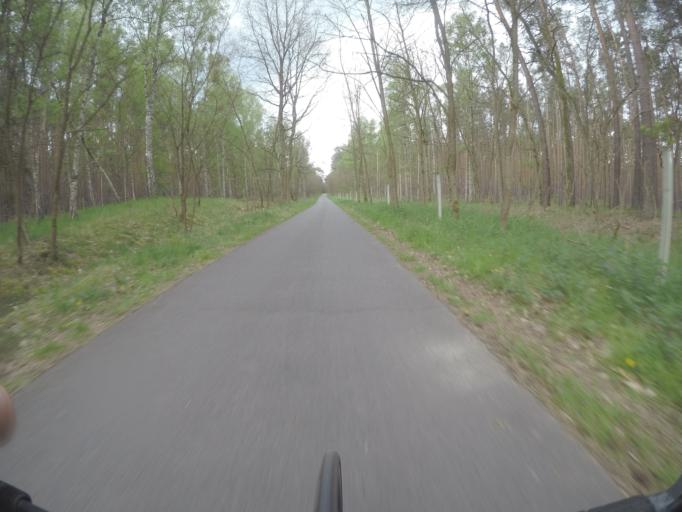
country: DE
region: Brandenburg
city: Biesenthal
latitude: 52.7864
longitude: 13.6369
